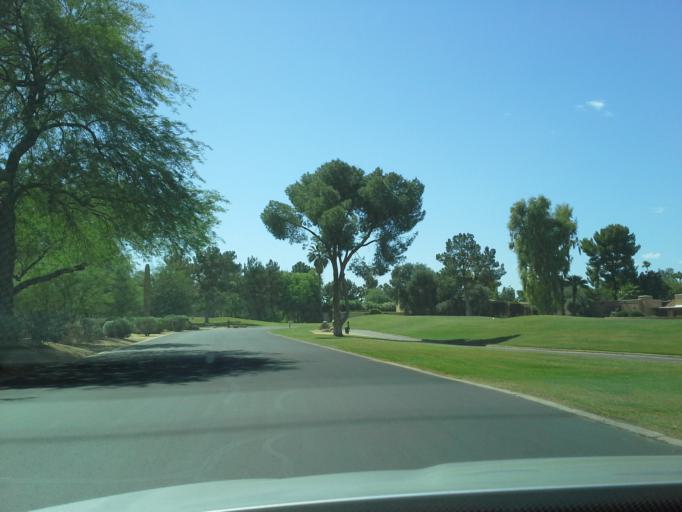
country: US
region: Arizona
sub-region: Maricopa County
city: Paradise Valley
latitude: 33.5585
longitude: -111.9297
